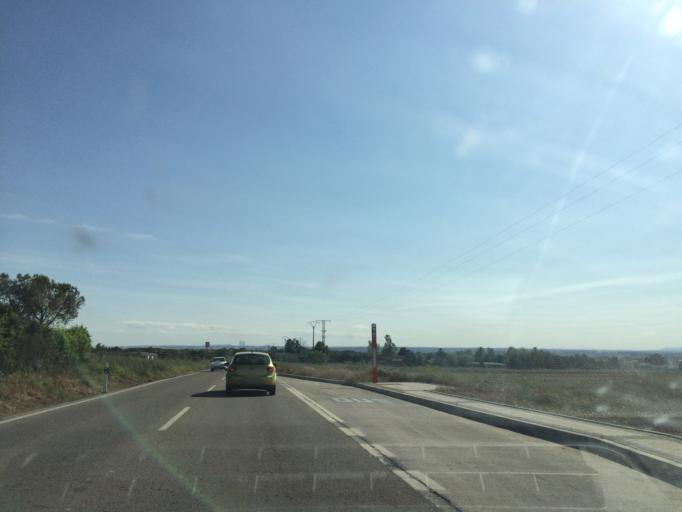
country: ES
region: Madrid
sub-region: Provincia de Madrid
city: Valdetorres de Jarama
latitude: 40.6648
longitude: -3.4826
